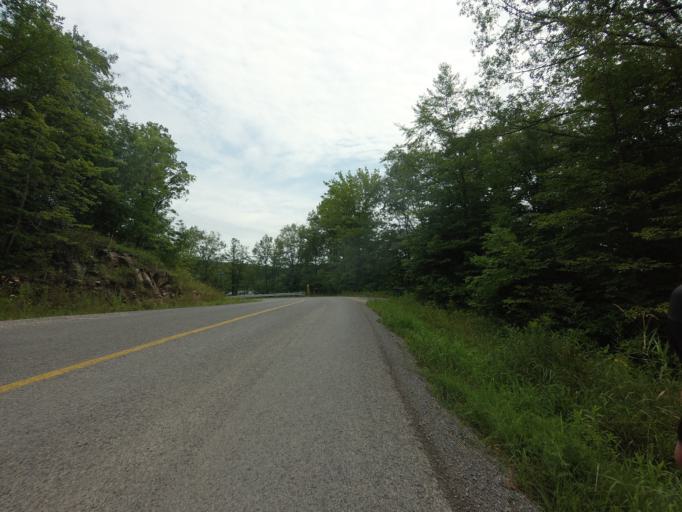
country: CA
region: Ontario
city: Kingston
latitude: 44.6491
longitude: -76.6551
